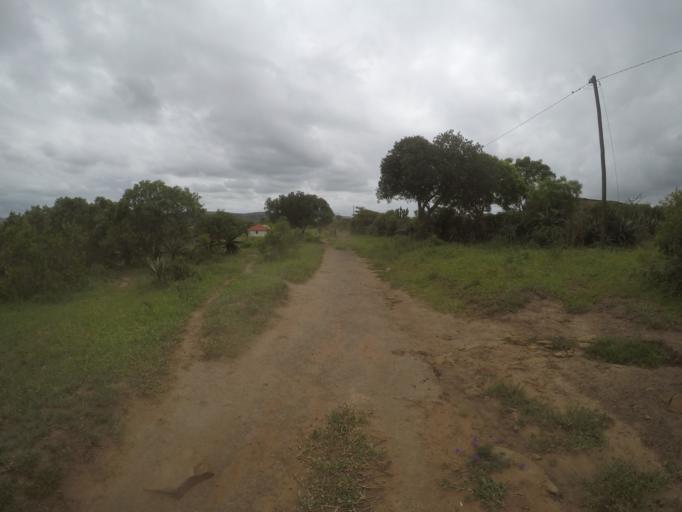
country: ZA
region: KwaZulu-Natal
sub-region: uThungulu District Municipality
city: Empangeni
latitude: -28.5948
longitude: 31.8475
